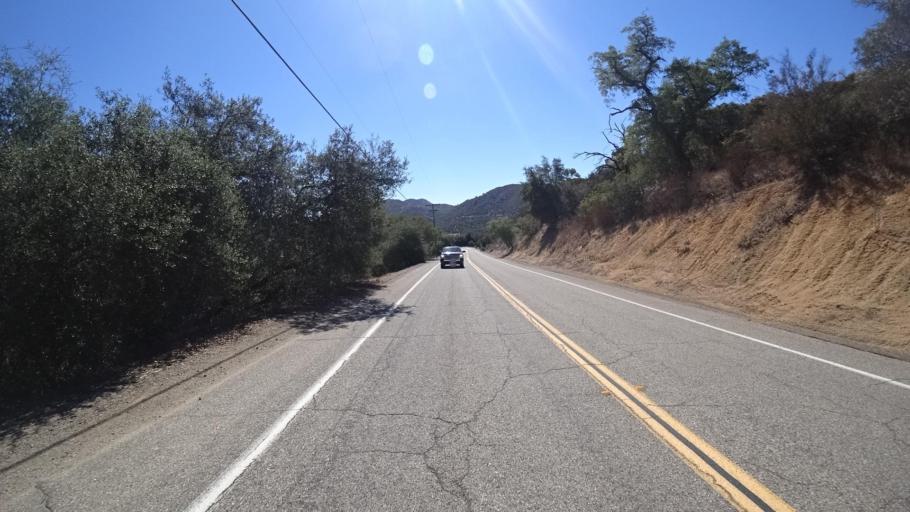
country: US
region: California
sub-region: San Diego County
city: Alpine
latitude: 32.7218
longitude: -116.7594
